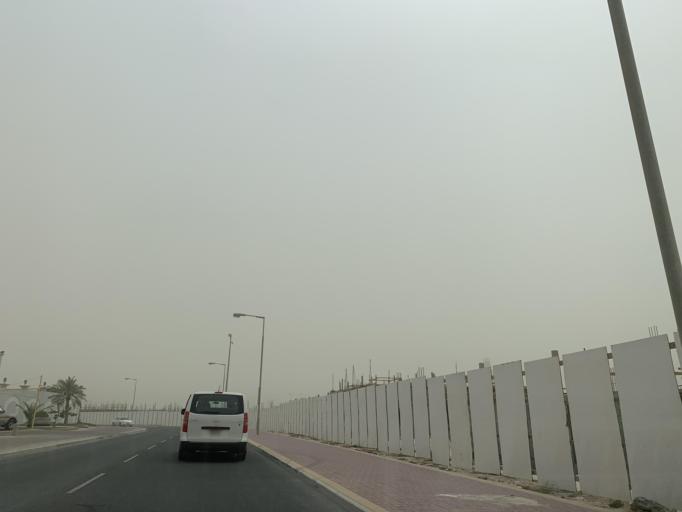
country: BH
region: Central Governorate
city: Madinat Hamad
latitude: 26.1276
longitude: 50.5078
